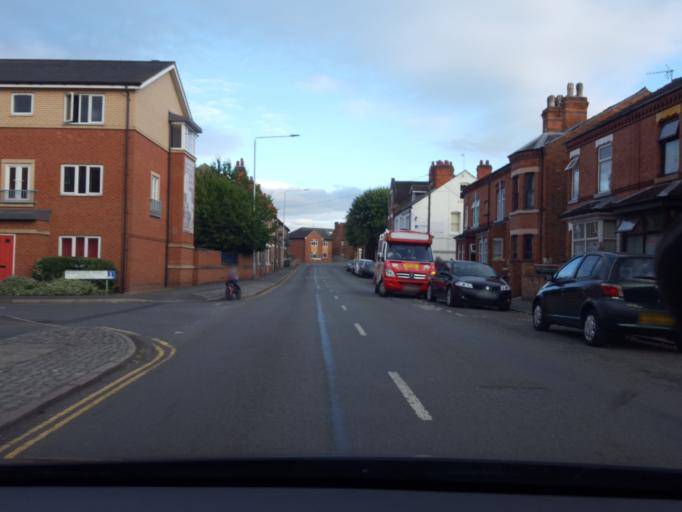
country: GB
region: England
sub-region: Leicestershire
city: Loughborough
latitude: 52.7750
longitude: -1.1979
